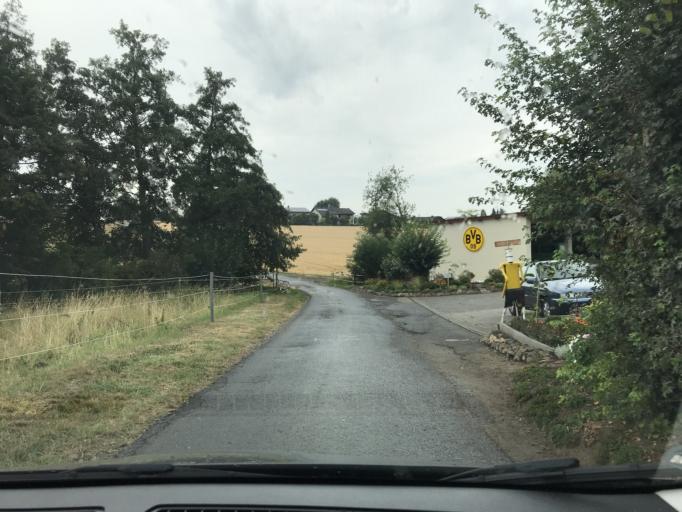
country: DE
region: Hesse
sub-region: Regierungsbezirk Darmstadt
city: Rossdorf
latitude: 49.8514
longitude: 8.7616
